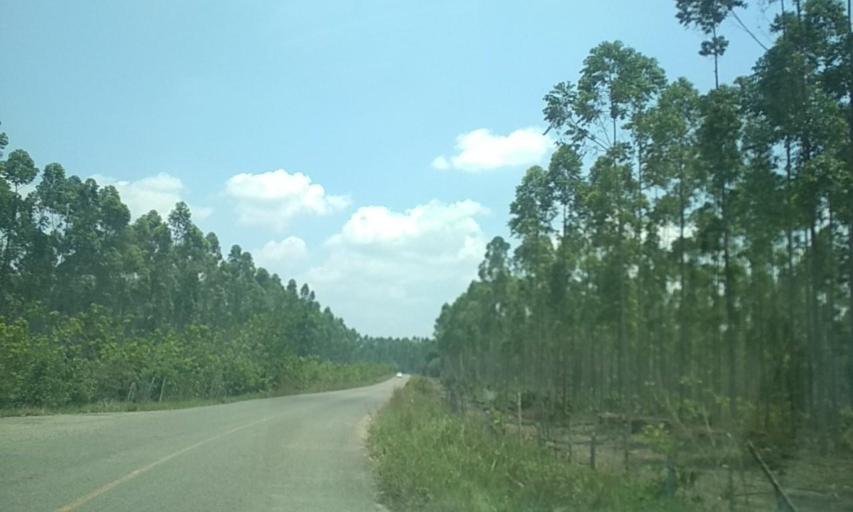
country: MX
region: Tabasco
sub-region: Huimanguillo
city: Francisco Rueda
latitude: 17.8383
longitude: -93.8835
